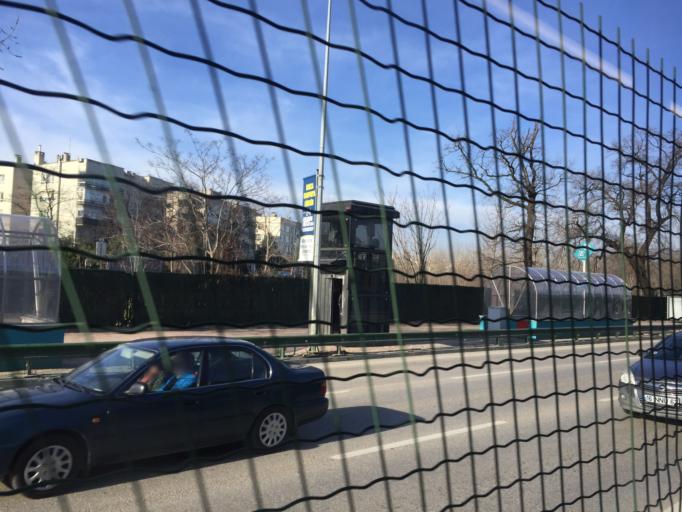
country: TR
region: Bursa
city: Yildirim
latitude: 40.2094
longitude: 29.0252
